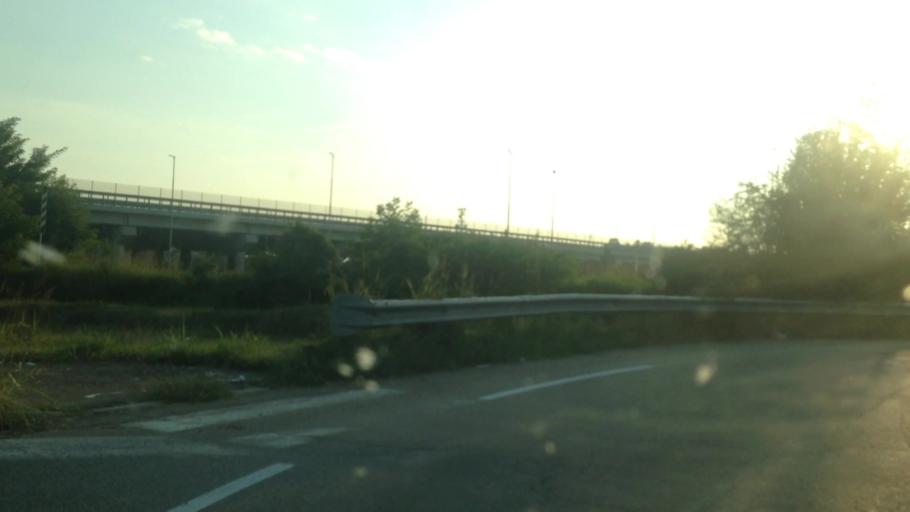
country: IT
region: Piedmont
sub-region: Provincia di Asti
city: Asti
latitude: 44.9147
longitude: 8.2291
